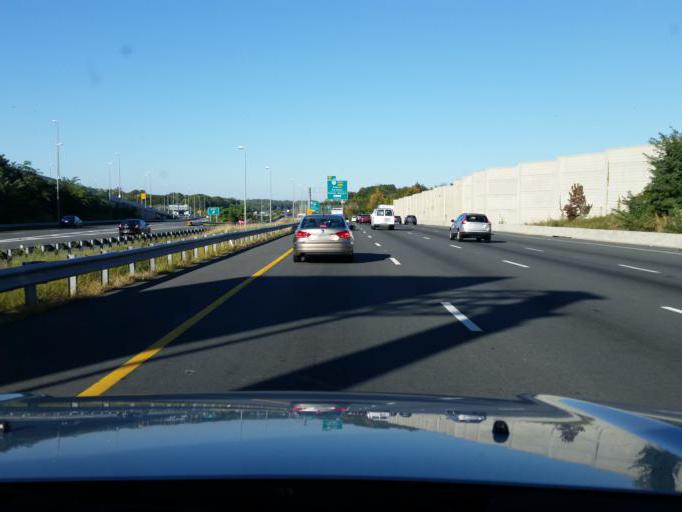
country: US
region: Virginia
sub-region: Fairfax County
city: Pimmit Hills
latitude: 38.9275
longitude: -77.2128
